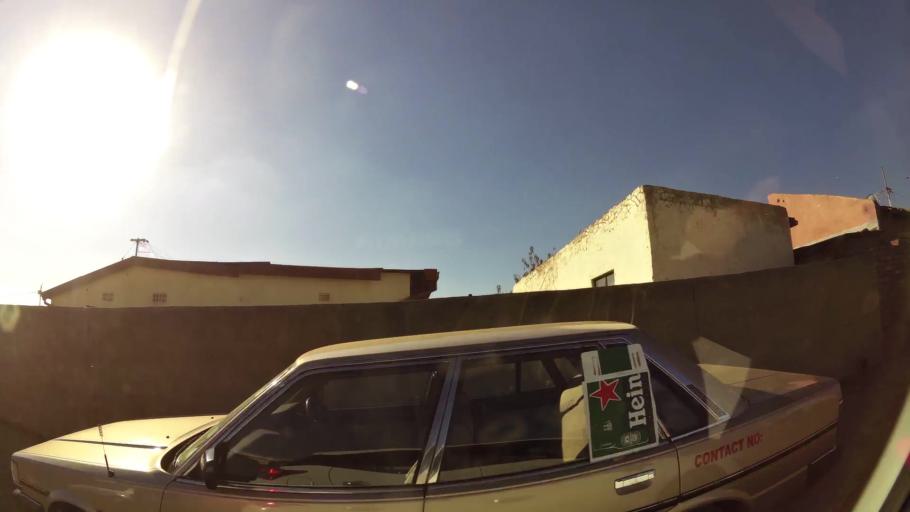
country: ZA
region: Gauteng
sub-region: City of Tshwane Metropolitan Municipality
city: Cullinan
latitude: -25.7221
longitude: 28.3819
